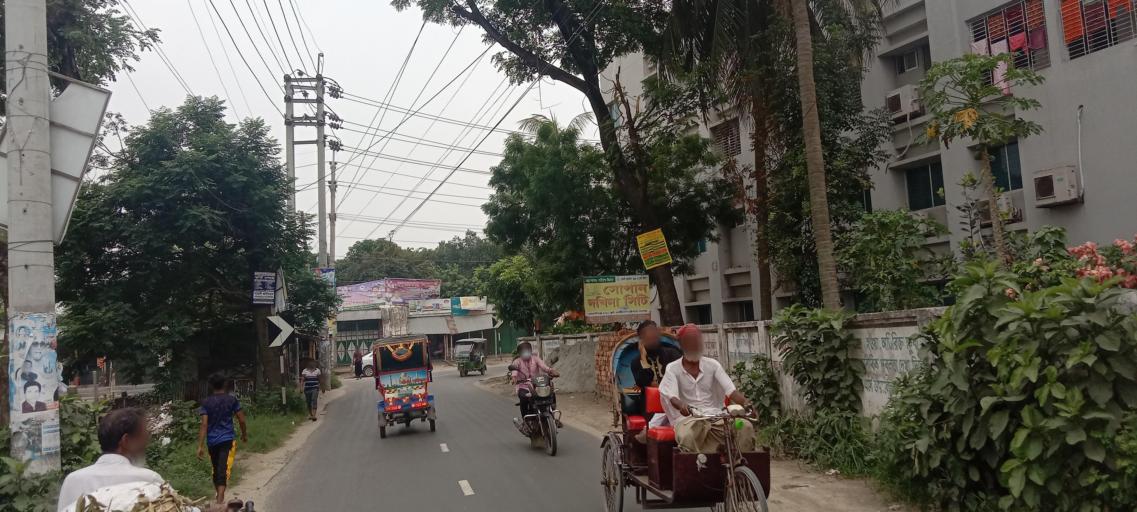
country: BD
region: Dhaka
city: Azimpur
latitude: 23.7067
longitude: 90.3478
